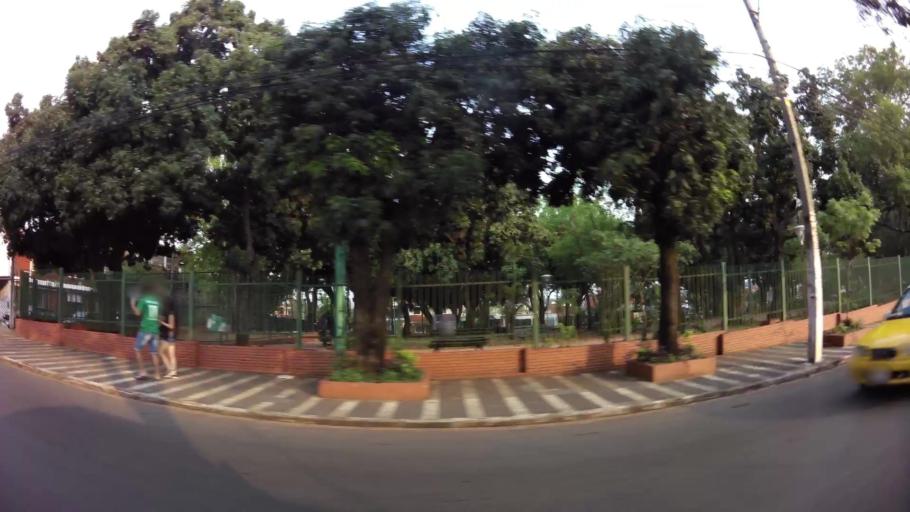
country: PY
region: Central
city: Lambare
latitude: -25.3249
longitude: -57.5815
